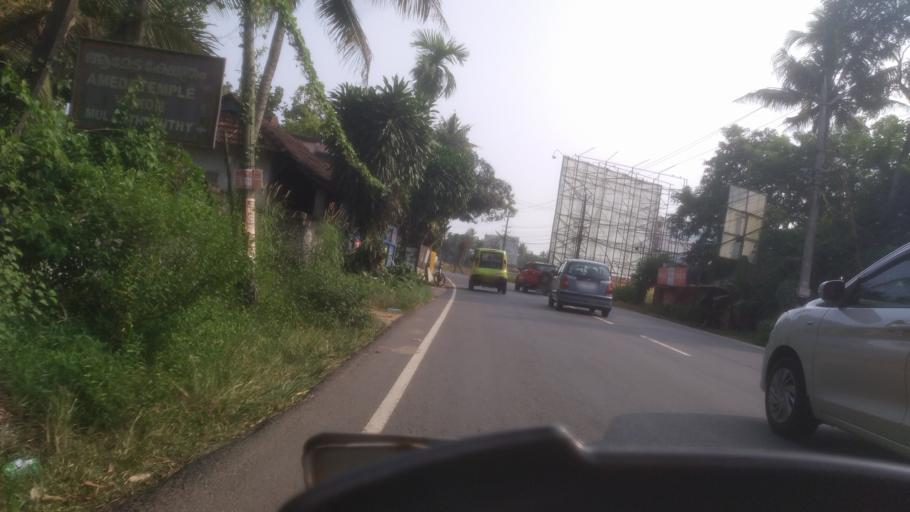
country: IN
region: Kerala
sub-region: Alappuzha
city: Arukutti
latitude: 9.9002
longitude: 76.3687
